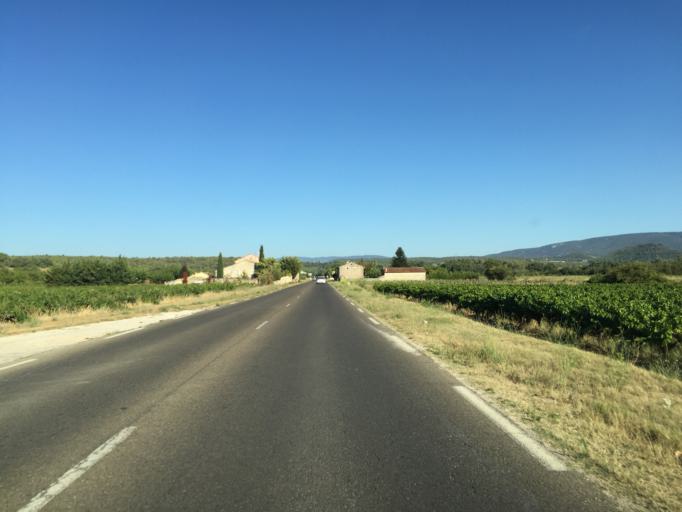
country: FR
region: Provence-Alpes-Cote d'Azur
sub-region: Departement du Vaucluse
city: Menerbes
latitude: 43.8610
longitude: 5.1838
